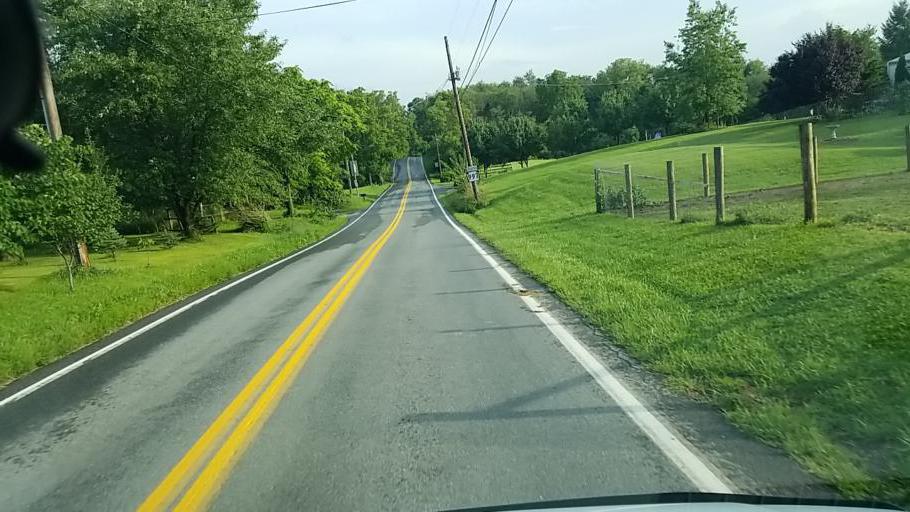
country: US
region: Pennsylvania
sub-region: Cumberland County
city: Newville
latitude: 40.2123
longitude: -77.4712
